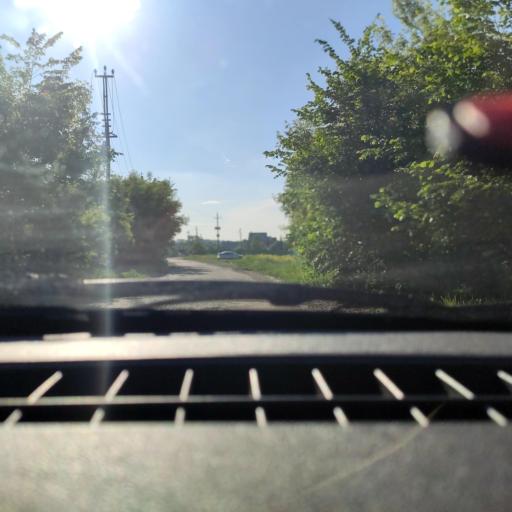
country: RU
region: Bashkortostan
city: Avdon
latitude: 54.4657
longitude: 55.8310
